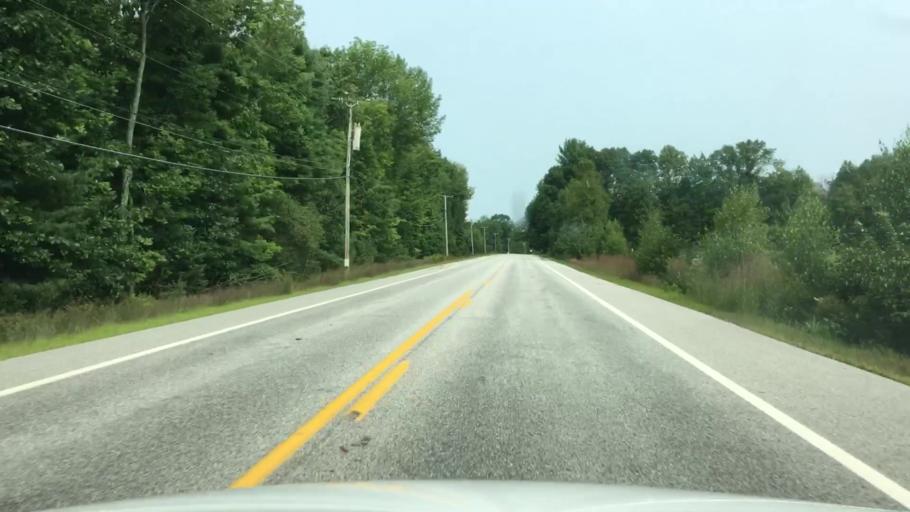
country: US
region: Maine
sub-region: Androscoggin County
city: Livermore Falls
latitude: 44.4256
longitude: -70.1454
